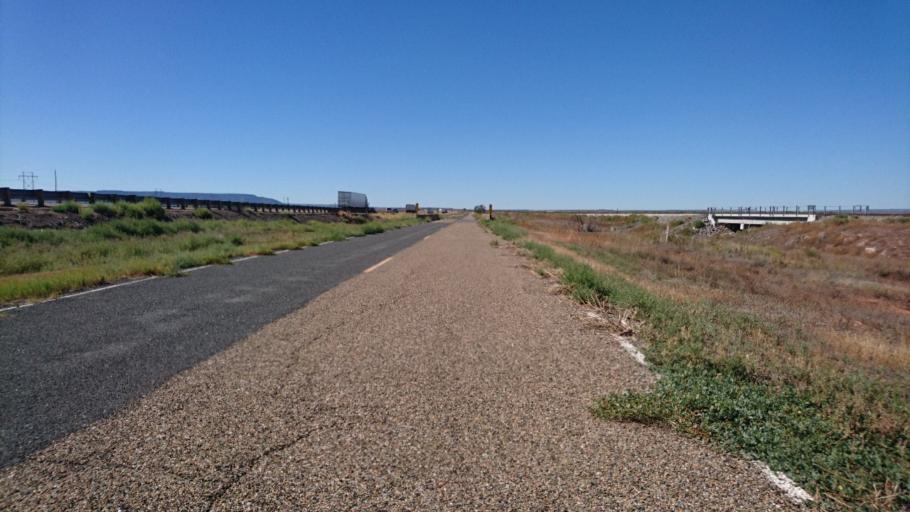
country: US
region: New Mexico
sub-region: Quay County
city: Tucumcari
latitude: 35.1036
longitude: -104.0371
